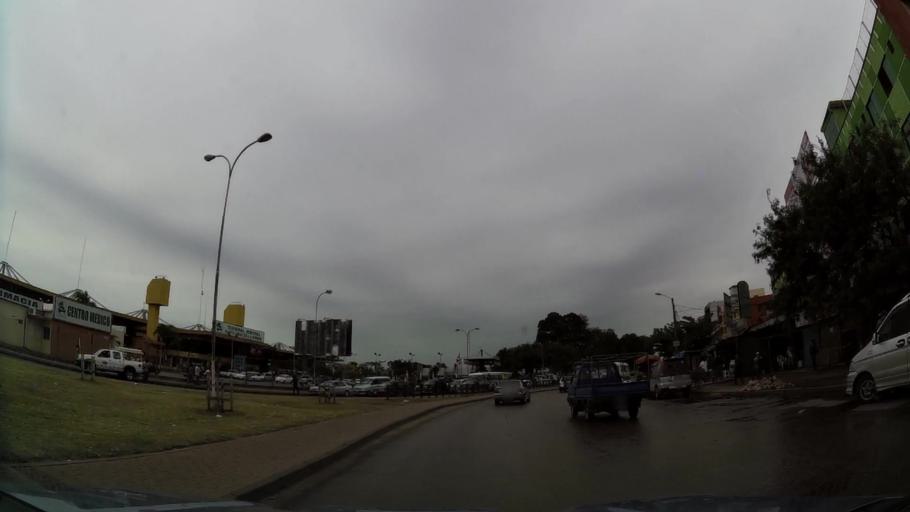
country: BO
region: Santa Cruz
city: Santa Cruz de la Sierra
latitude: -17.7891
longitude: -63.1619
